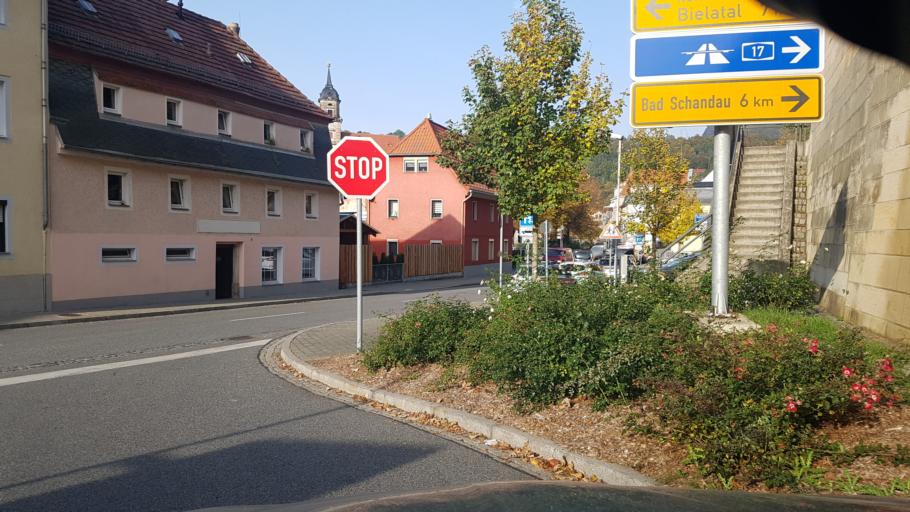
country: DE
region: Saxony
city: Konigstein
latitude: 50.9162
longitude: 14.0723
